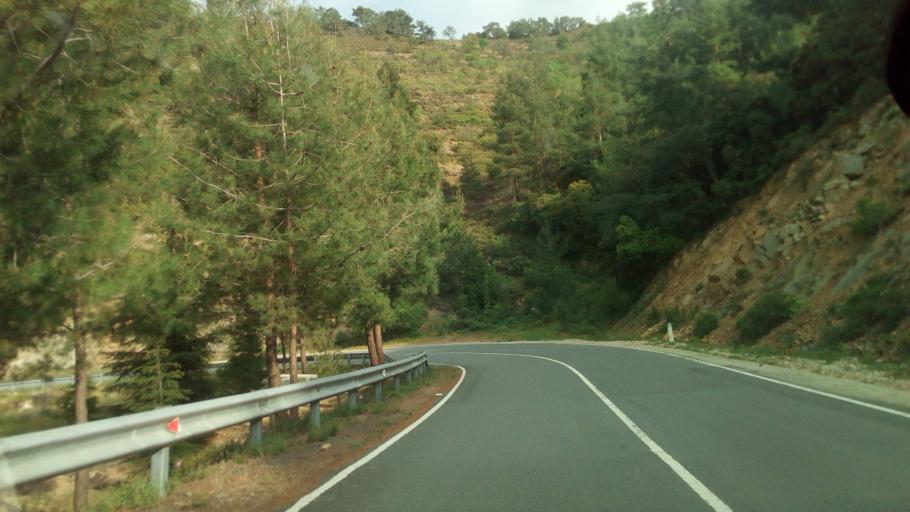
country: CY
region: Lefkosia
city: Kakopetria
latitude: 35.0001
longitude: 32.7965
